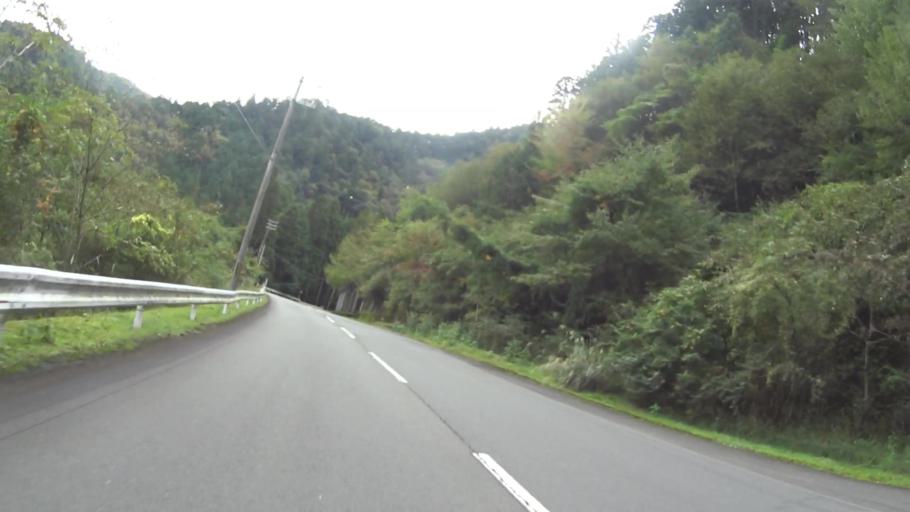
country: JP
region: Fukui
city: Obama
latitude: 35.3163
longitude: 135.6512
